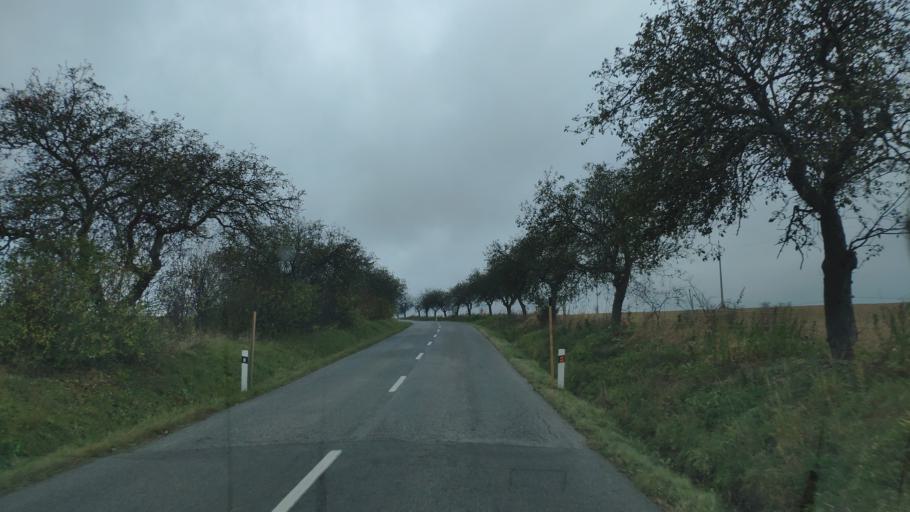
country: SK
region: Presovsky
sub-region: Okres Presov
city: Presov
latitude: 49.0976
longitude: 21.2231
